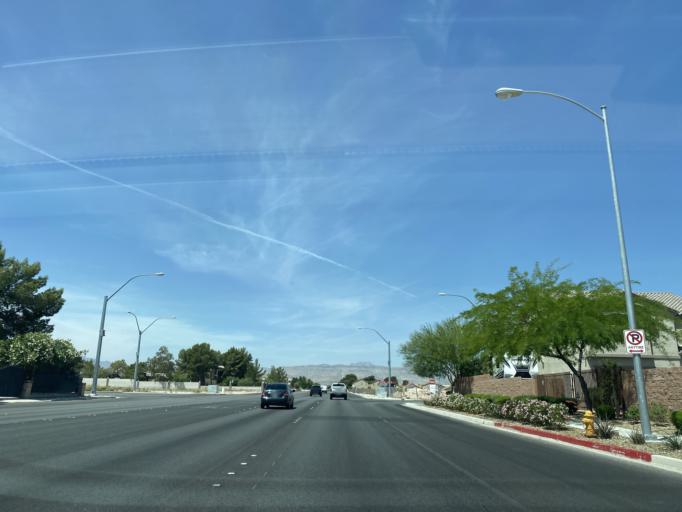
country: US
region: Nevada
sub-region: Clark County
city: Spring Valley
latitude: 36.0853
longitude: -115.2331
